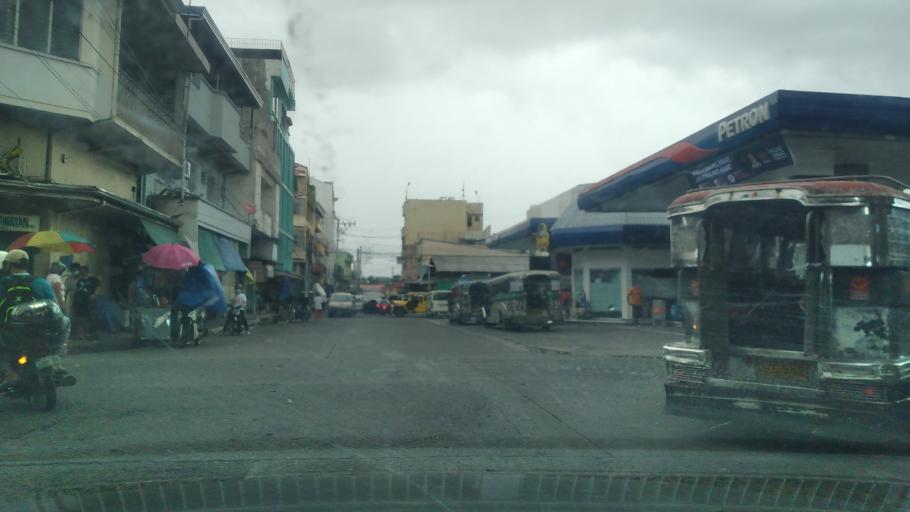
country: PH
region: Calabarzon
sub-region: Province of Quezon
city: Lucena
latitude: 13.9342
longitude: 121.6134
